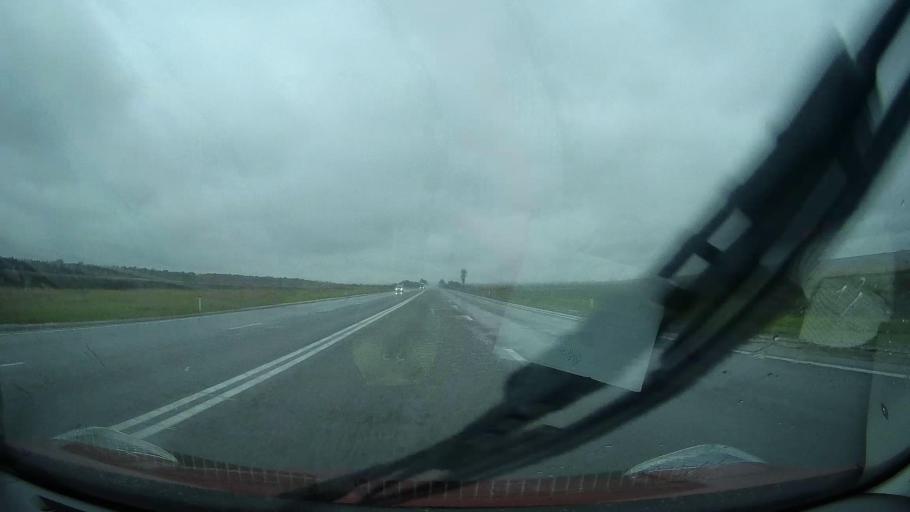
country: RU
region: Stavropol'skiy
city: Nevinnomyssk
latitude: 44.6280
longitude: 42.0435
